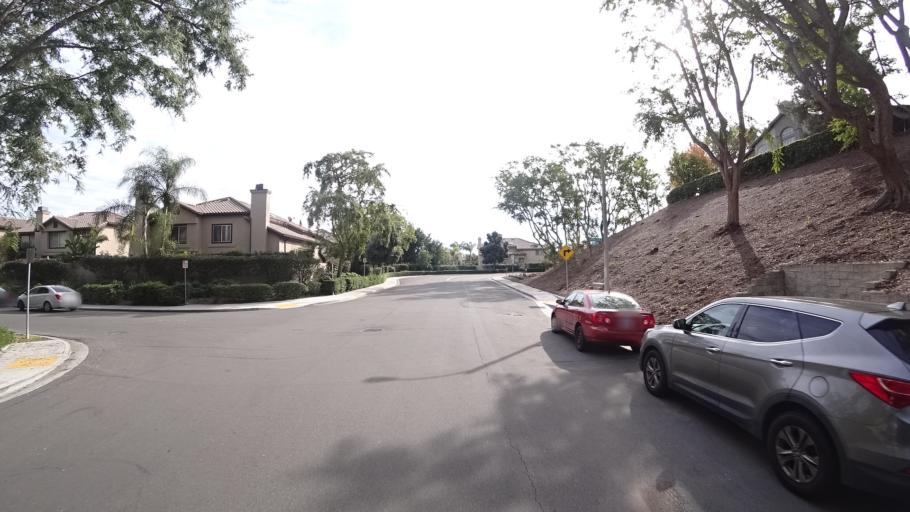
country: US
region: California
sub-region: Orange County
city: Aliso Viejo
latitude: 33.5753
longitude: -117.7197
